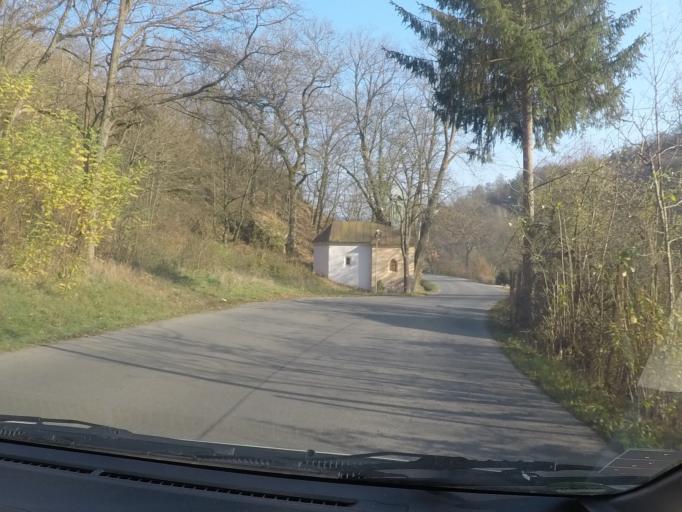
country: SK
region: Banskobystricky
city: Zarnovica
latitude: 48.4610
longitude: 18.7391
